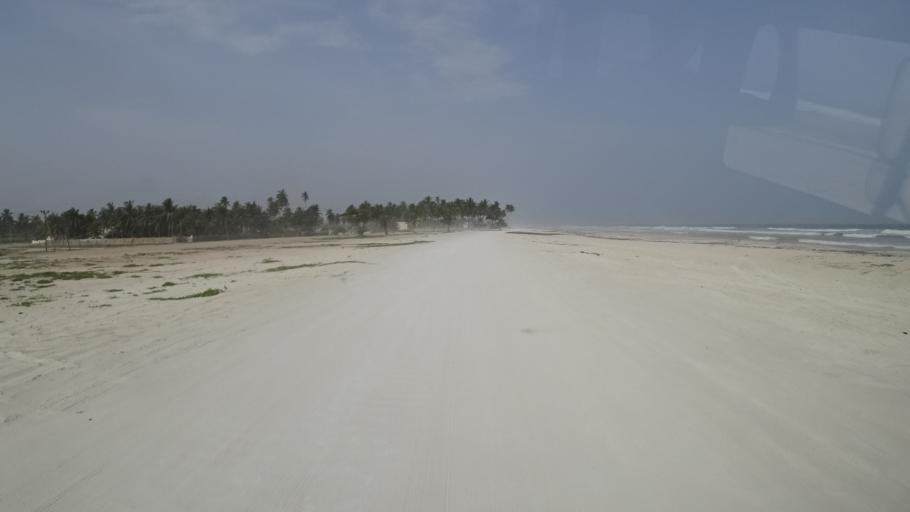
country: OM
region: Zufar
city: Salalah
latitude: 17.0024
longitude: 54.1197
